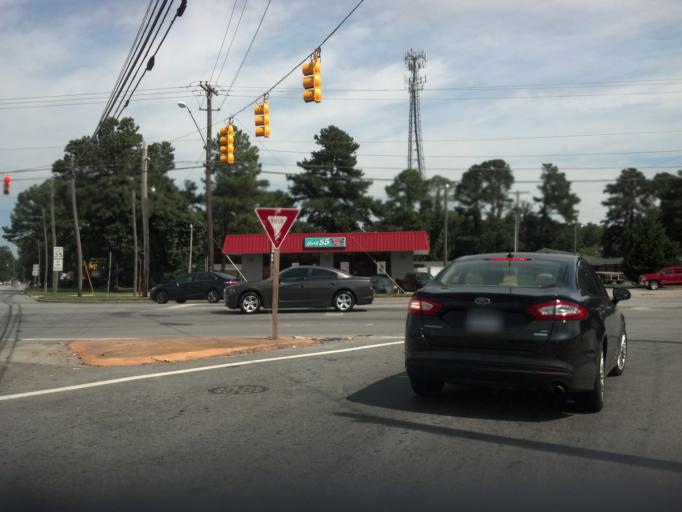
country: US
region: North Carolina
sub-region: Pitt County
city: Farmville
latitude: 35.5812
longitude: -77.5933
